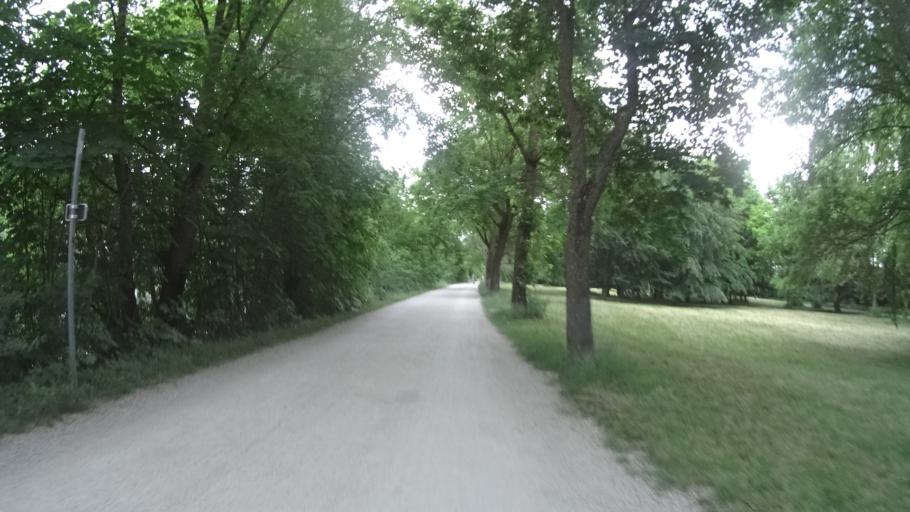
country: DE
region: Bavaria
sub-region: Upper Palatinate
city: Lappersdorf
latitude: 49.0302
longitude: 12.0676
